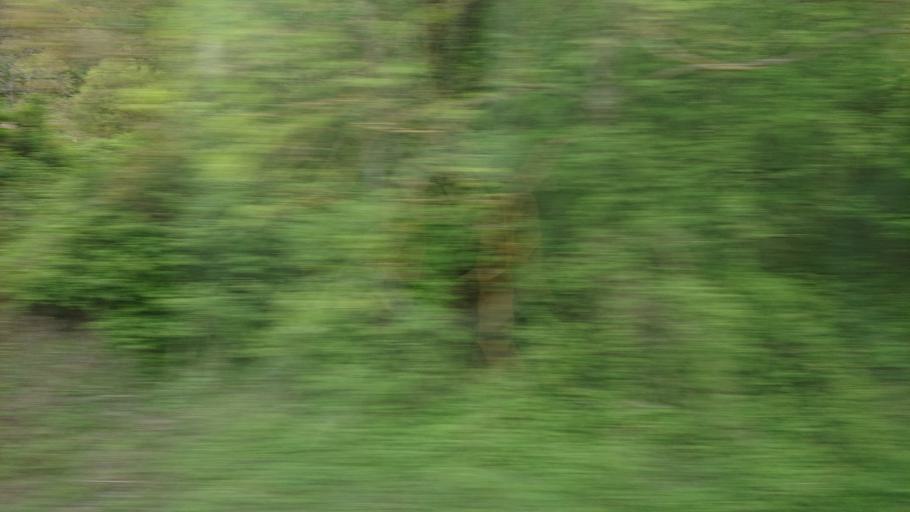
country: FR
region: Rhone-Alpes
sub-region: Departement de l'Ain
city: Collonges
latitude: 46.1176
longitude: 5.8899
